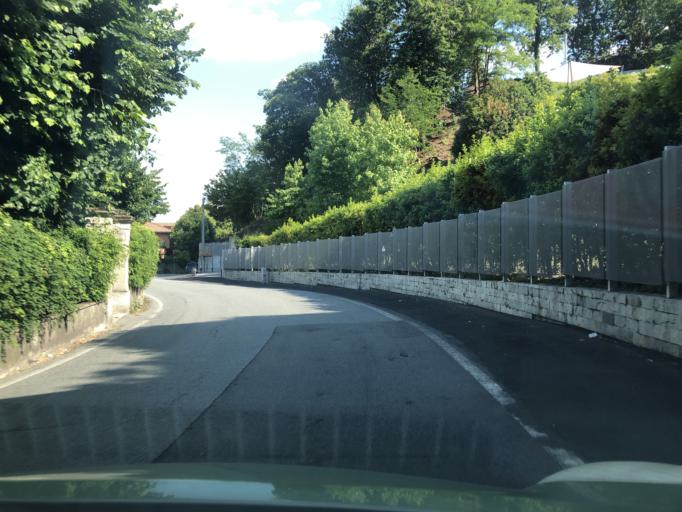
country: IT
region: Piedmont
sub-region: Provincia di Novara
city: Meina
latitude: 45.7721
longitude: 8.5416
